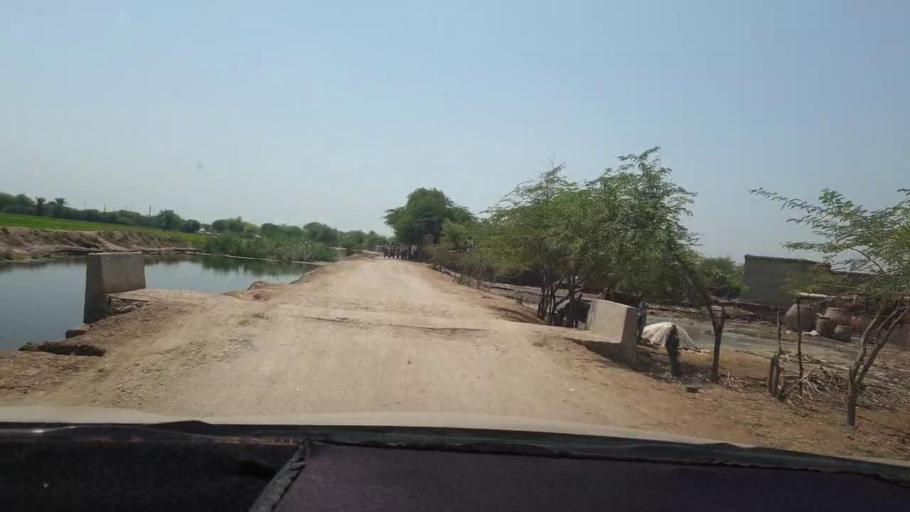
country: PK
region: Sindh
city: Shahdadkot
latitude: 27.8376
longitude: 67.9408
